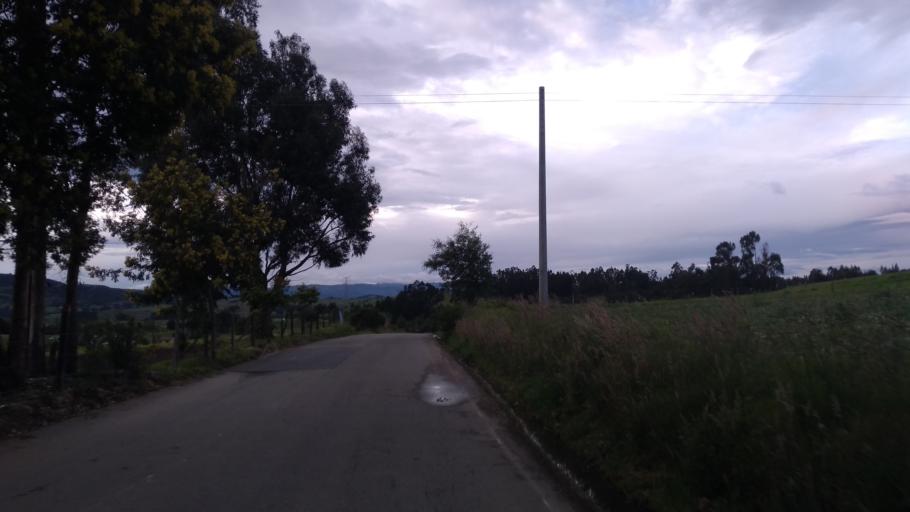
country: CO
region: Boyaca
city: Toca
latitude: 5.5908
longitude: -73.1812
